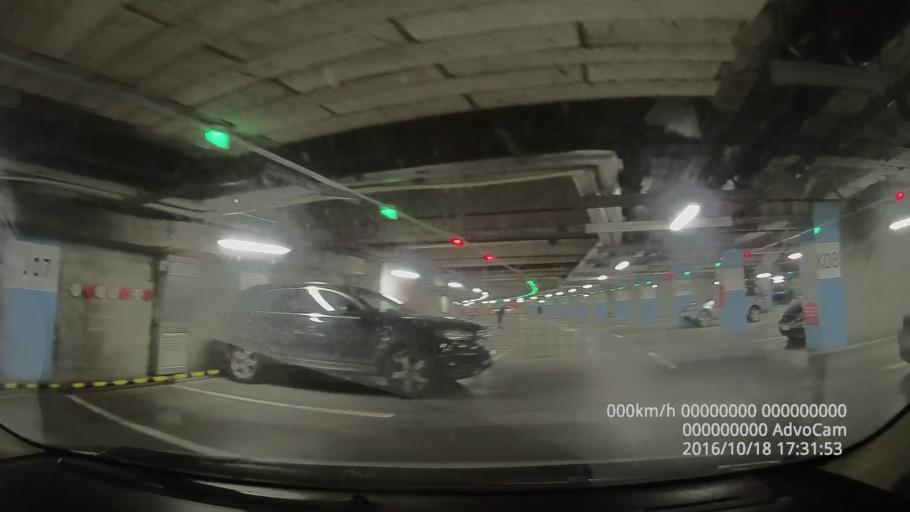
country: RO
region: Ilfov
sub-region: Comuna Otopeni
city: Otopeni
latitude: 44.5045
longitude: 26.0888
